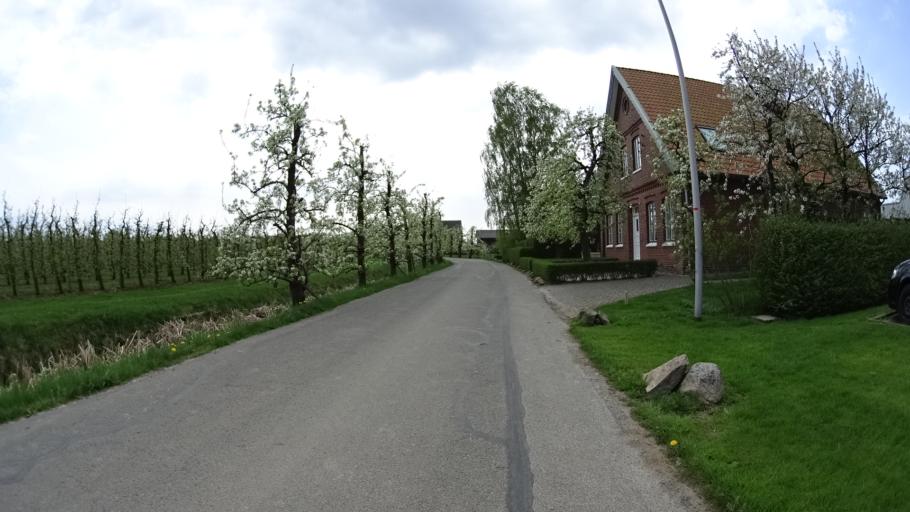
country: DE
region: Lower Saxony
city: Jork
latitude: 53.5356
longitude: 9.7386
